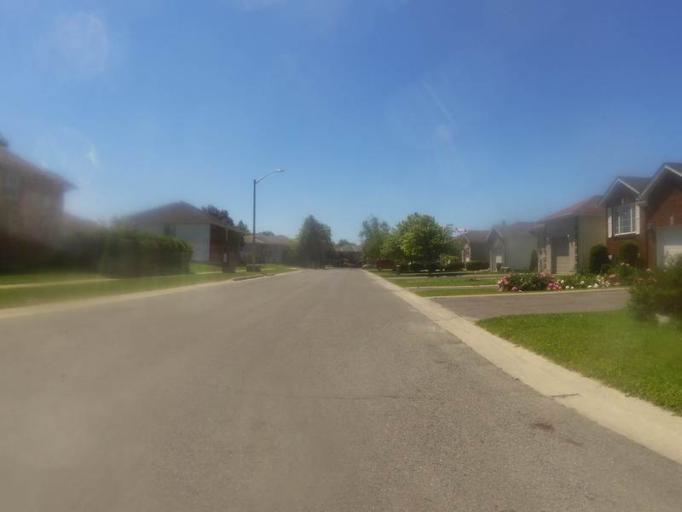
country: CA
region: Ontario
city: Kingston
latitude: 44.2619
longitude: -76.5561
